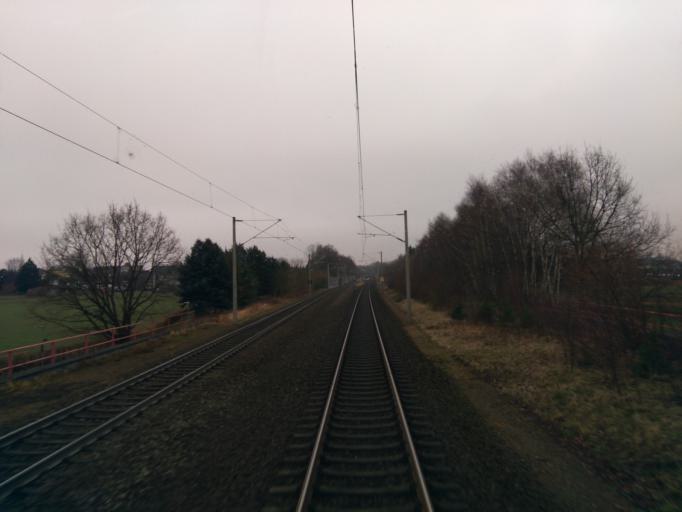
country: DE
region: Lower Saxony
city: Seevetal
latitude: 53.4005
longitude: 9.9714
